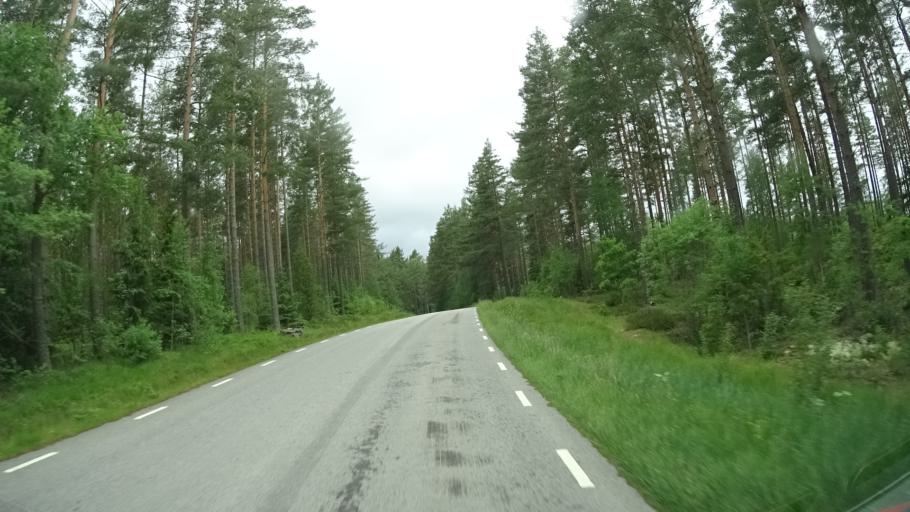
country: SE
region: Joenkoeping
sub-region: Eksjo Kommun
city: Mariannelund
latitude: 57.6993
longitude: 15.6540
